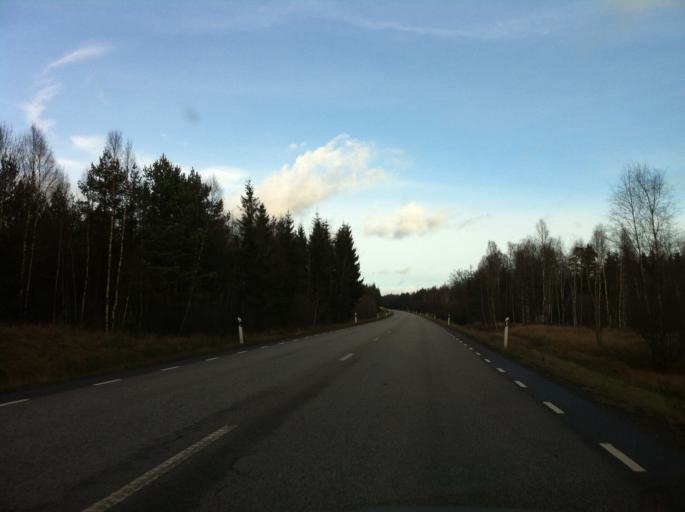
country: SE
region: Kronoberg
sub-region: Almhults Kommun
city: AElmhult
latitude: 56.5867
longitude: 14.1920
